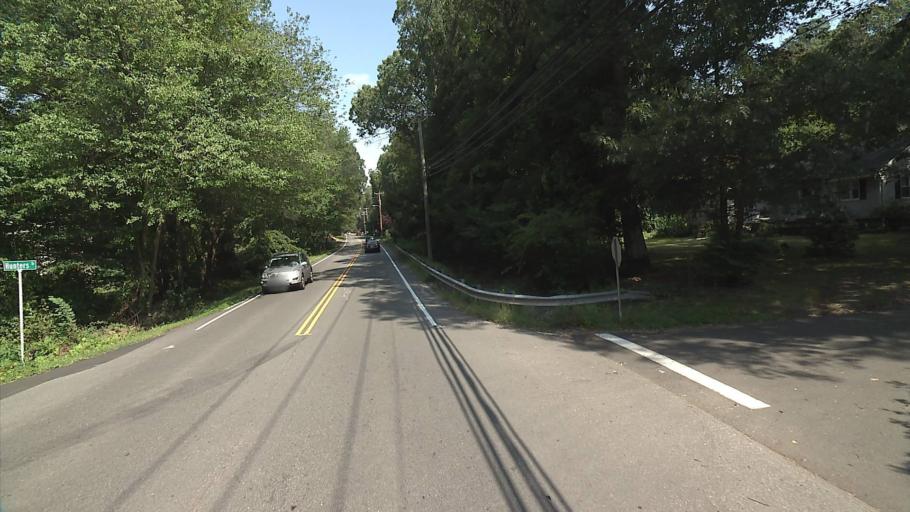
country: US
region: Connecticut
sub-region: New Haven County
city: Madison Center
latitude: 41.2903
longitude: -72.6024
